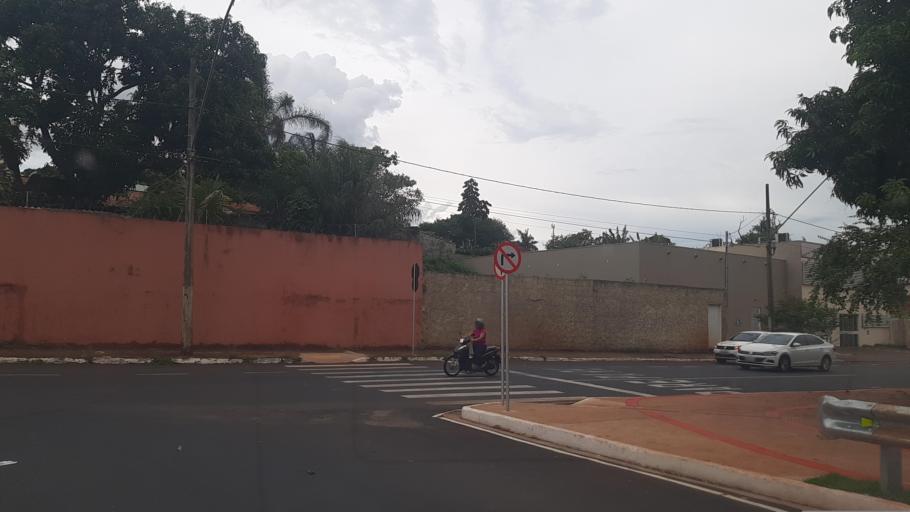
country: BR
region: Minas Gerais
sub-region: Uberlandia
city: Uberlandia
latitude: -18.9218
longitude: -48.2989
